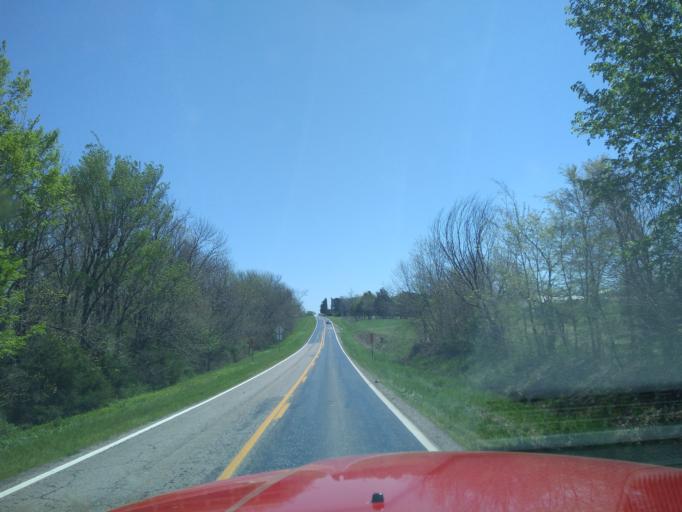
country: US
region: Arkansas
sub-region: Washington County
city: West Fork
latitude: 35.9048
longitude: -94.2325
